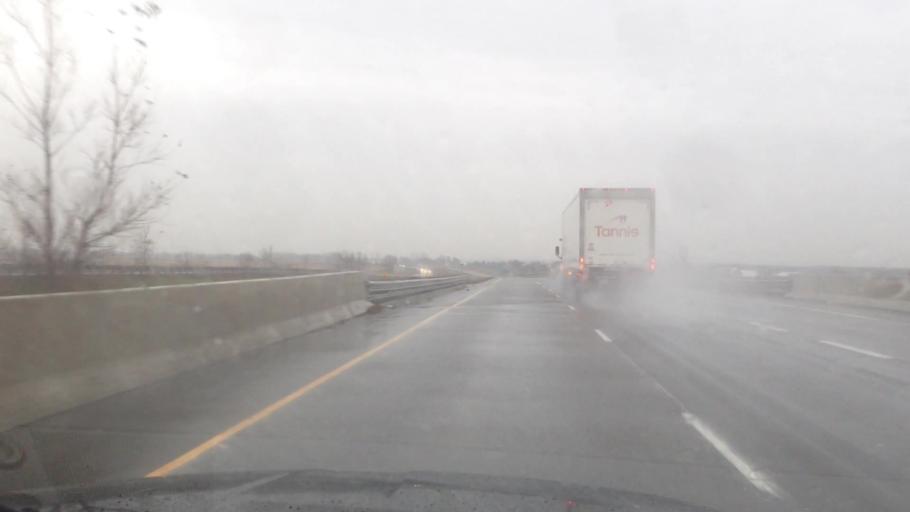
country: CA
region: Ontario
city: Casselman
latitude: 45.3039
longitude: -75.0690
